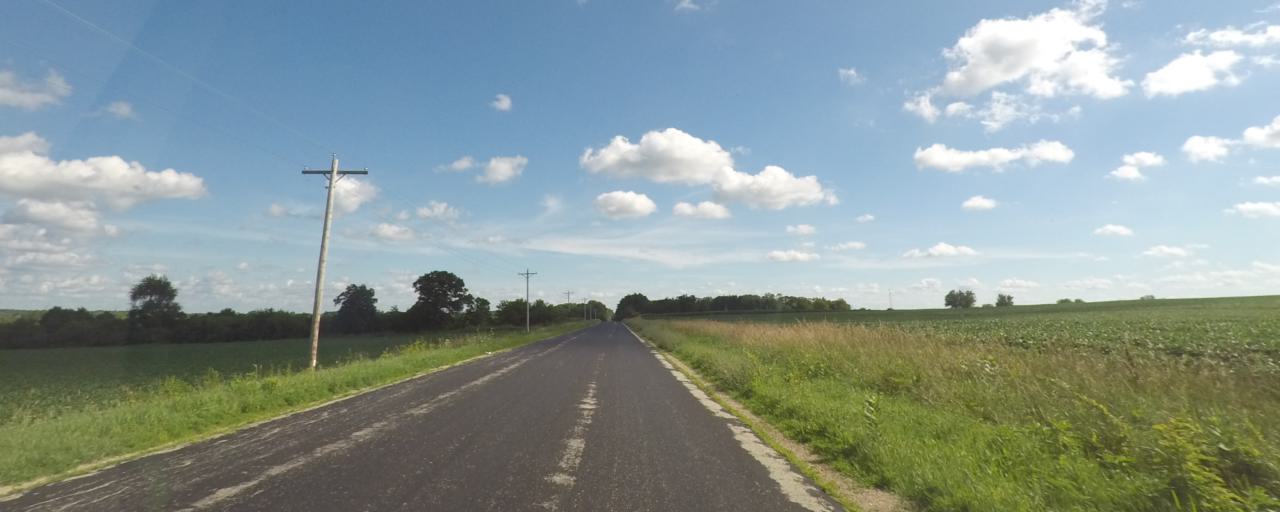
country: US
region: Wisconsin
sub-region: Rock County
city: Edgerton
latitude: 42.8586
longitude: -89.1320
